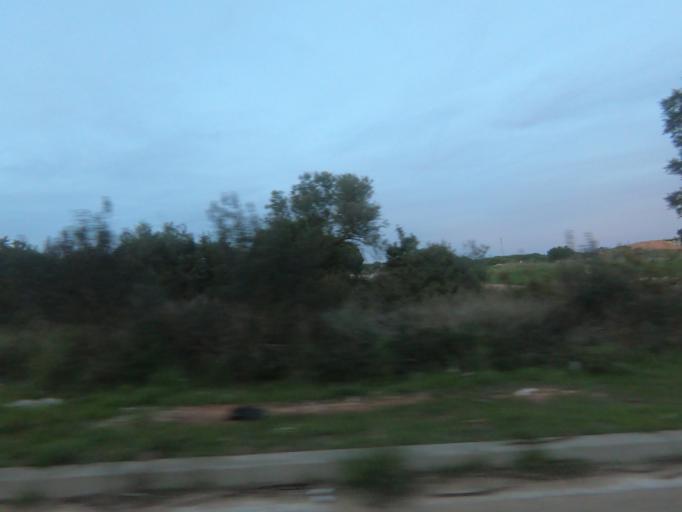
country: PT
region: Setubal
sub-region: Setubal
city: Setubal
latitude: 38.5161
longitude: -8.8585
